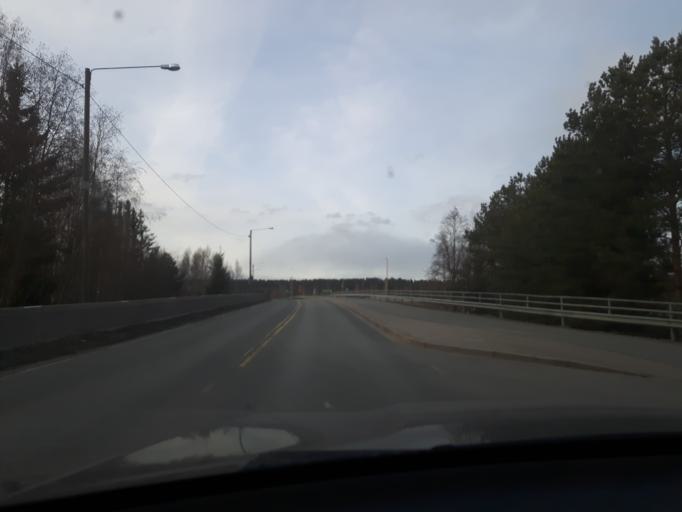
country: FI
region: Pirkanmaa
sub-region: Tampere
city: Kangasala
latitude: 61.4621
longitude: 24.0365
